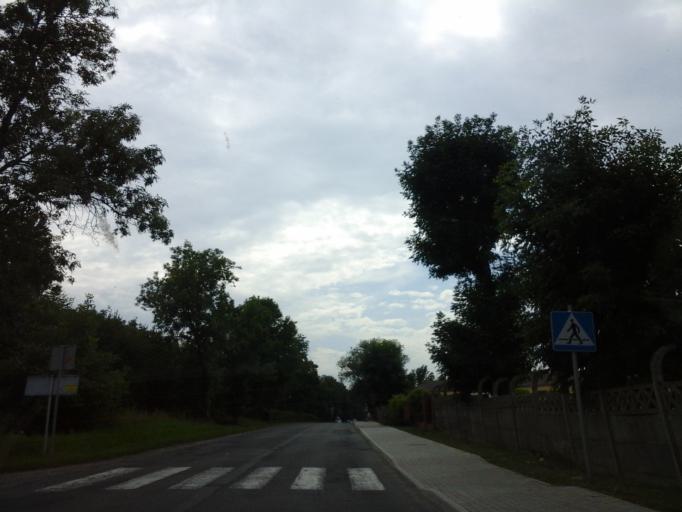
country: PL
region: Lower Silesian Voivodeship
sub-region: Powiat zabkowicki
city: Zabkowice Slaskie
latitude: 50.6004
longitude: 16.8222
